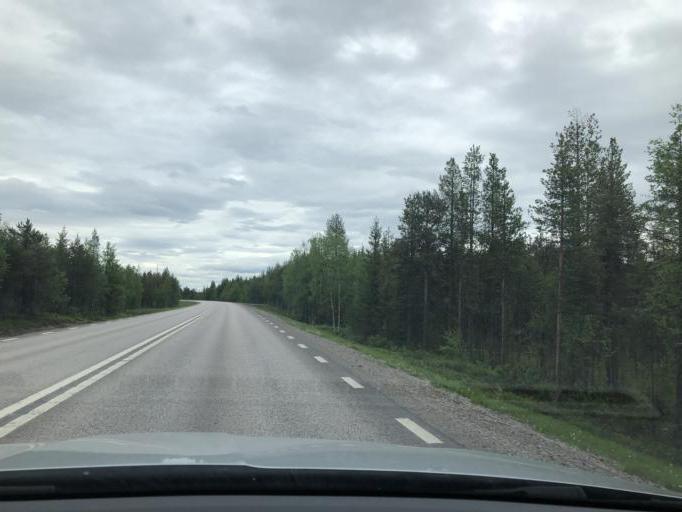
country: SE
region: Norrbotten
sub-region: Gallivare Kommun
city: Malmberget
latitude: 67.6447
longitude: 21.1235
